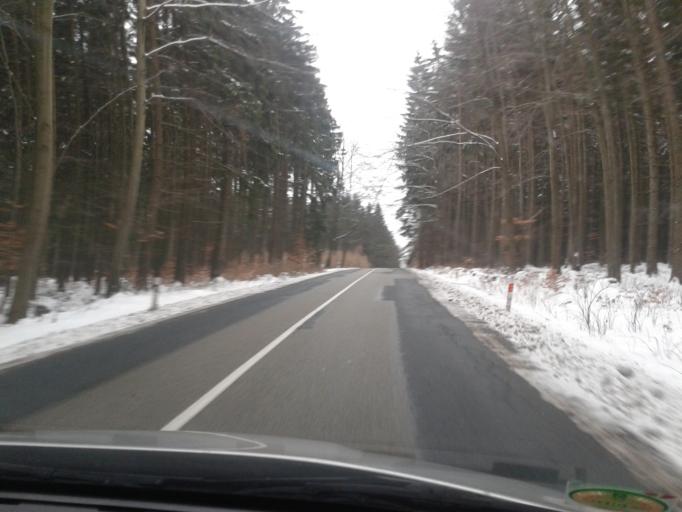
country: CZ
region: Olomoucky
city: Protivanov
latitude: 49.4732
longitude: 16.7855
